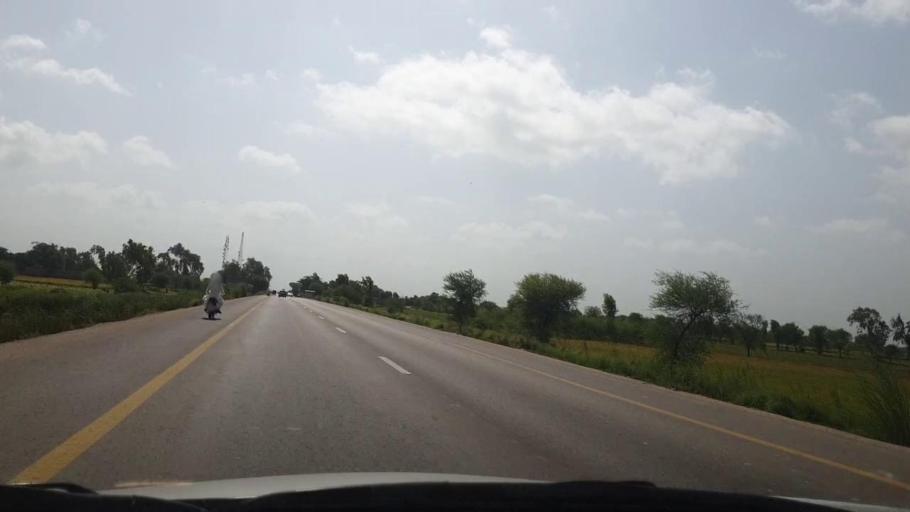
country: PK
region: Sindh
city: Matli
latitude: 24.9446
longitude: 68.7000
